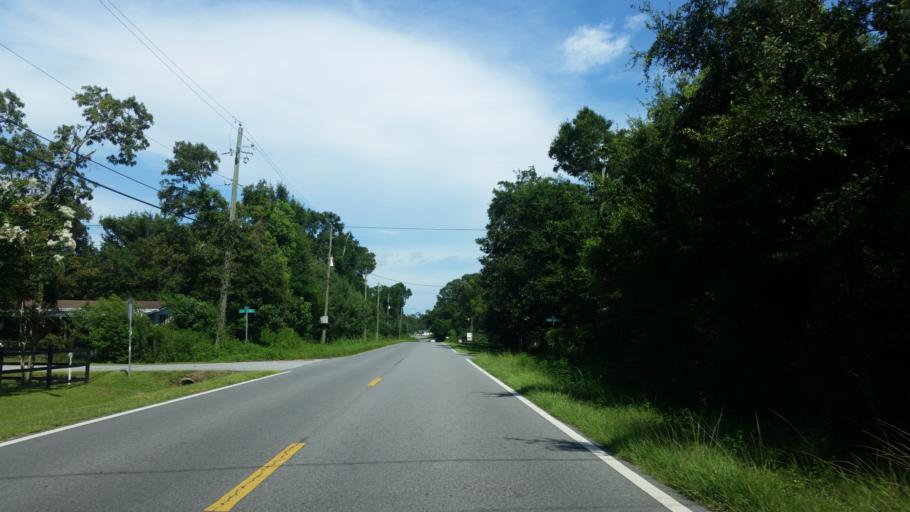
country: US
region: Florida
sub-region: Santa Rosa County
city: Pace
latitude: 30.5910
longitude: -87.1661
